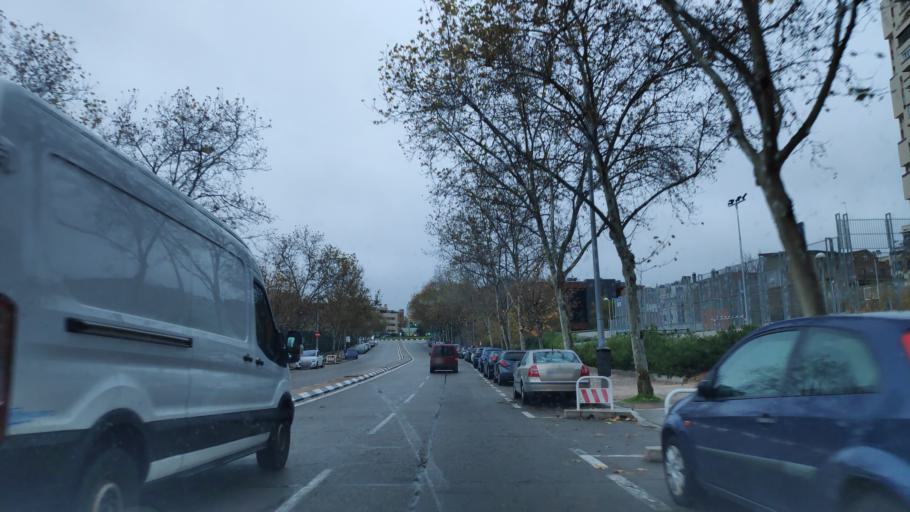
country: ES
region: Madrid
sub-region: Provincia de Madrid
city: Ciudad Lineal
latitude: 40.4593
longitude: -3.6428
